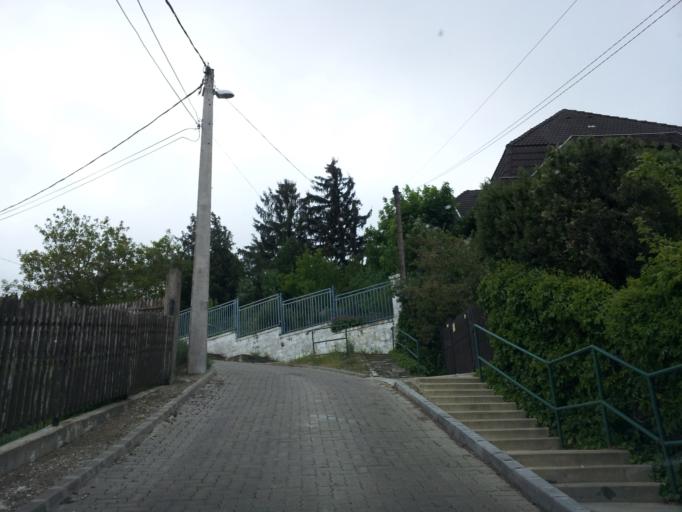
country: HU
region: Budapest
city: Budapest XXII. keruelet
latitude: 47.4386
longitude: 19.0205
